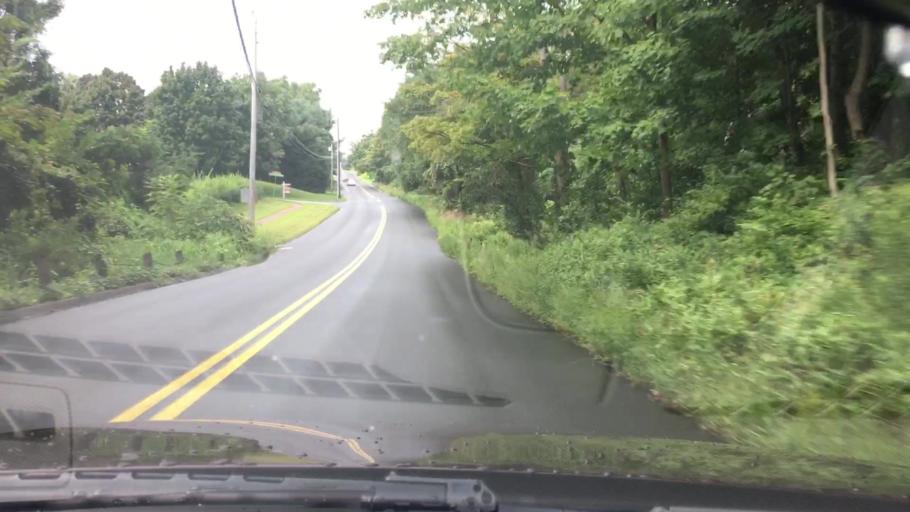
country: US
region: Connecticut
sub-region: Hartford County
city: Manchester
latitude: 41.7359
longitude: -72.5359
